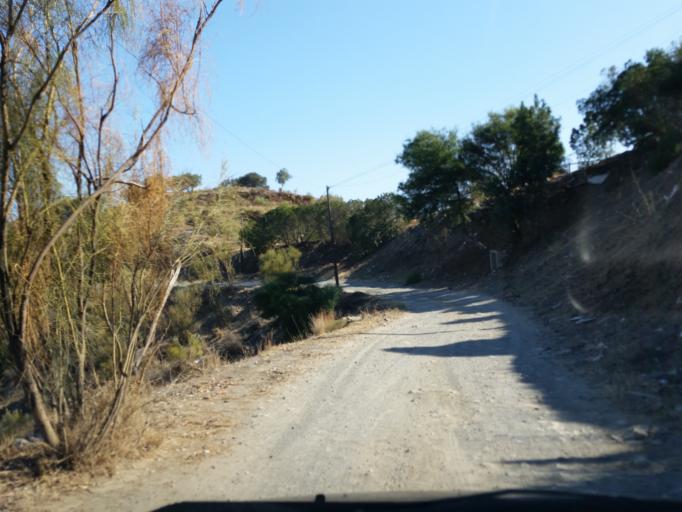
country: ES
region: Andalusia
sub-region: Provincia de Malaga
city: Mijas
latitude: 36.5795
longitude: -4.6083
